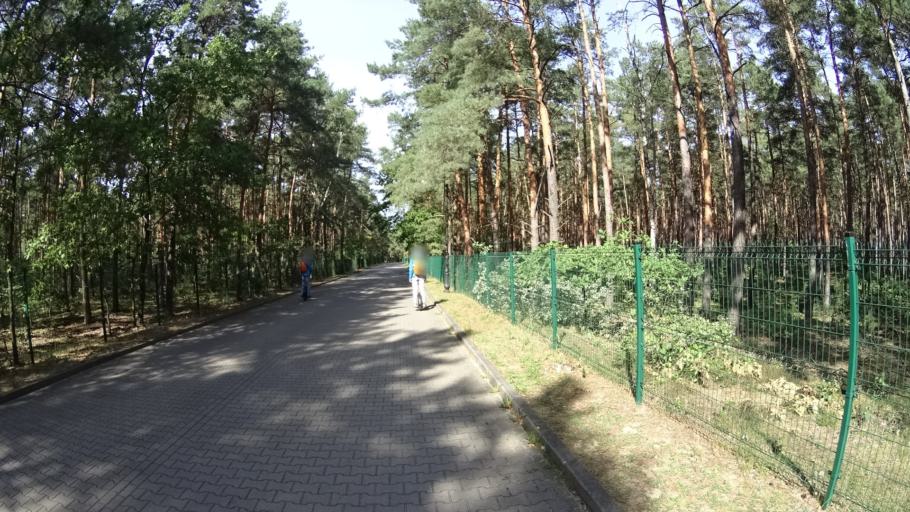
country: PL
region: Masovian Voivodeship
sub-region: Powiat legionowski
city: Bialobrzegi
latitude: 52.4586
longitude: 21.0746
